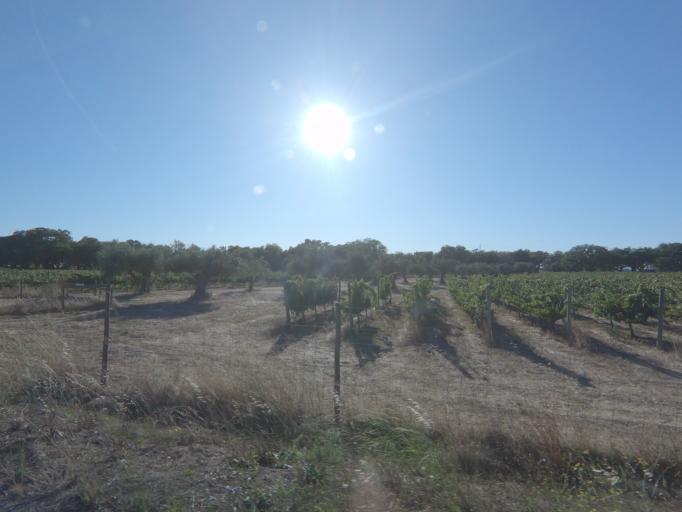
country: PT
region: Setubal
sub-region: Palmela
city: Quinta do Anjo
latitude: 38.5426
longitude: -8.9852
